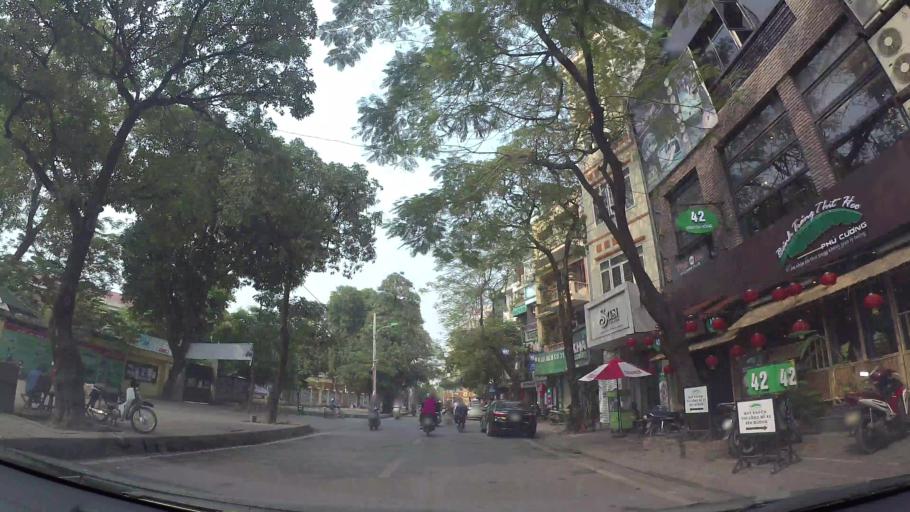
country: VN
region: Ha Noi
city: Cau Giay
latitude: 21.0161
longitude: 105.8100
